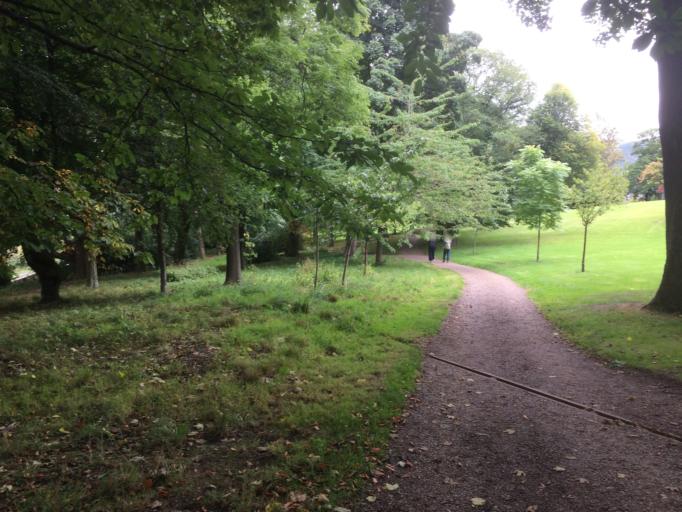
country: GB
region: Scotland
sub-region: Edinburgh
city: Edinburgh
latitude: 55.9560
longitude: -3.1787
